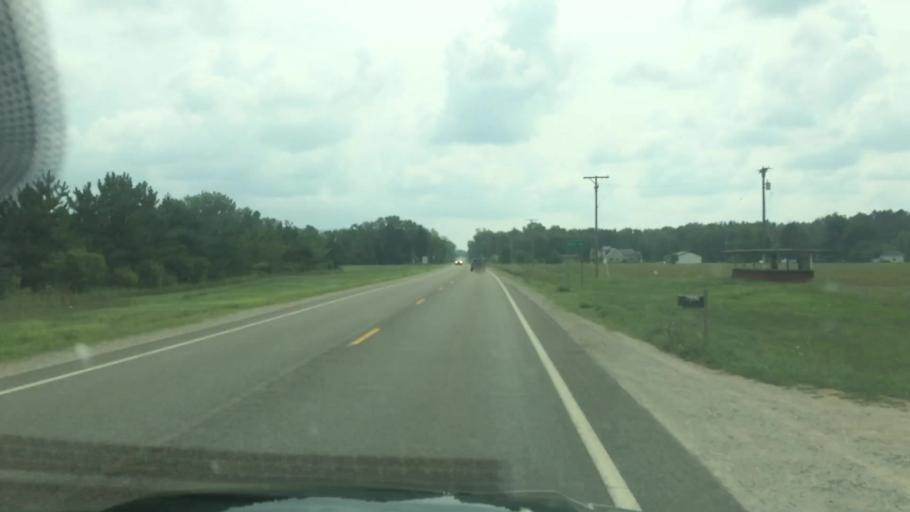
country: US
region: Michigan
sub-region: Tuscola County
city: Cass City
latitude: 43.6491
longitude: -83.0983
